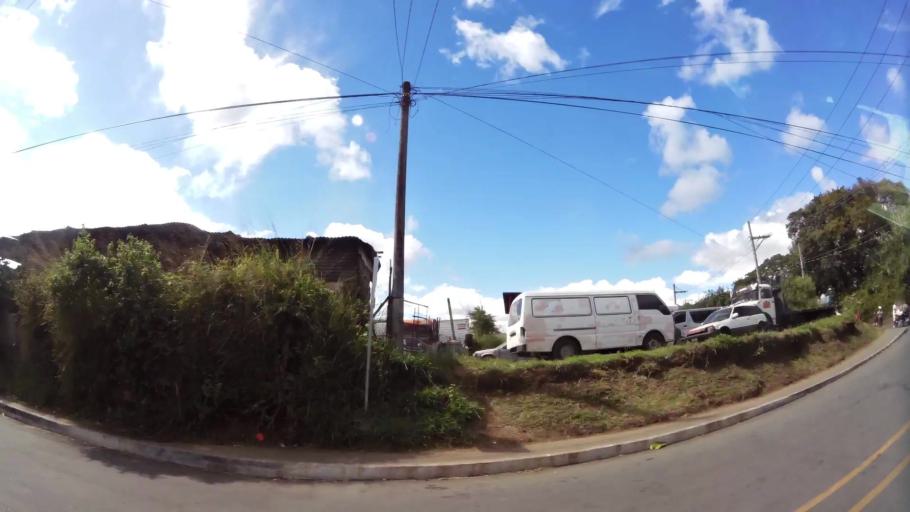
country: GT
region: Guatemala
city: Santa Catarina Pinula
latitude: 14.5566
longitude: -90.5427
